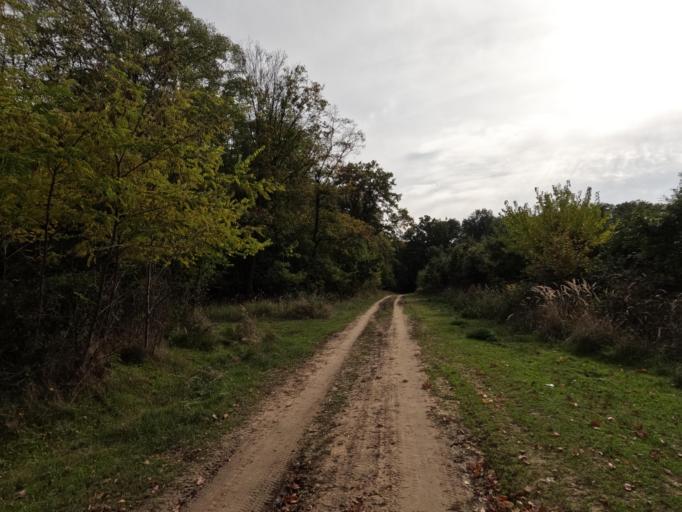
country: HU
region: Tolna
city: Szentgalpuszta
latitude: 46.3204
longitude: 18.6526
